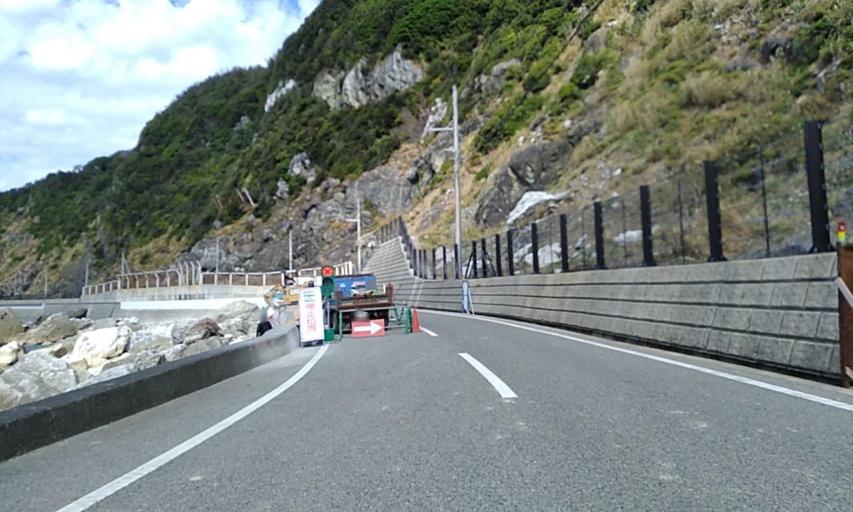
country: JP
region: Wakayama
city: Gobo
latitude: 33.9746
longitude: 135.0764
